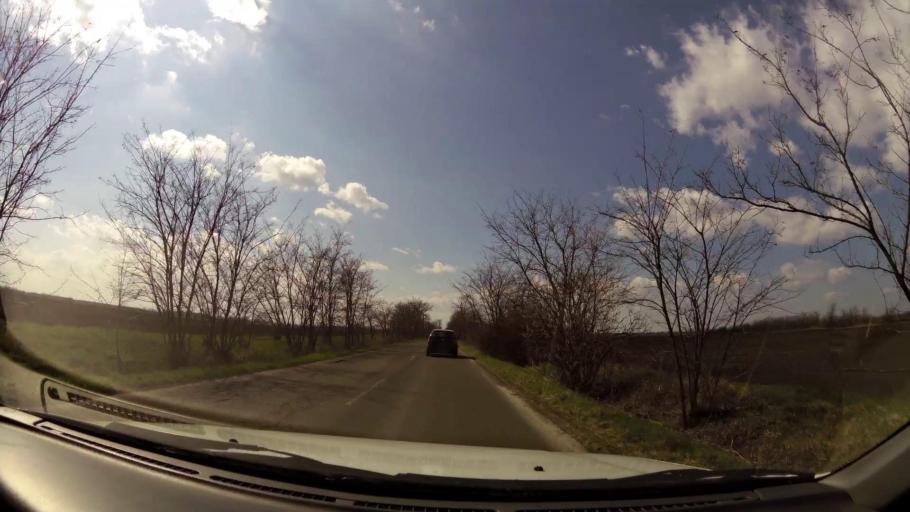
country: HU
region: Pest
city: Tapioszele
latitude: 47.3354
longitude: 19.9082
